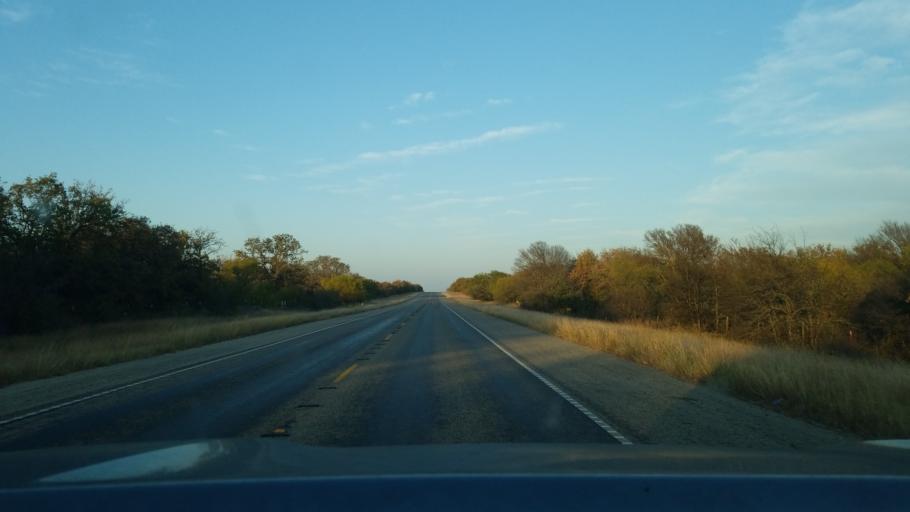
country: US
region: Texas
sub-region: Eastland County
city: Cisco
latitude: 32.4252
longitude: -98.9323
